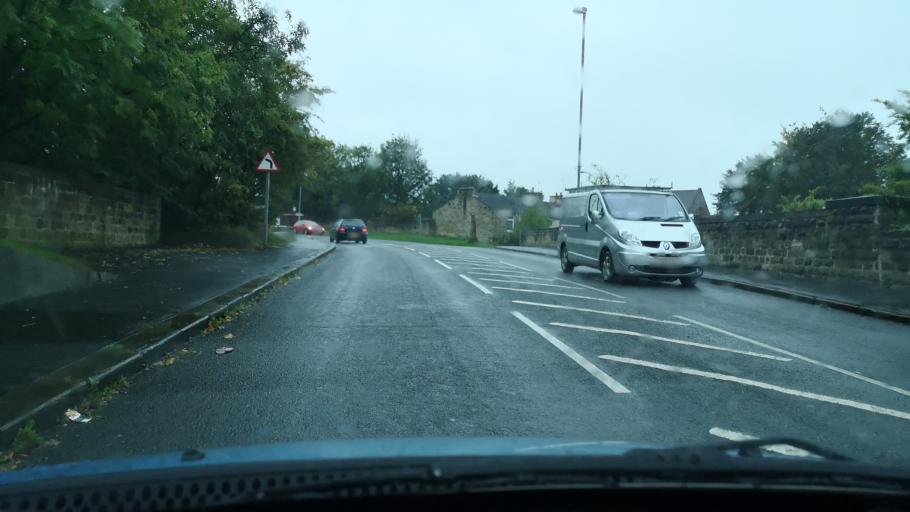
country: GB
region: England
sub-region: City and Borough of Wakefield
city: Low Ackworth
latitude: 53.6437
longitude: -1.3368
